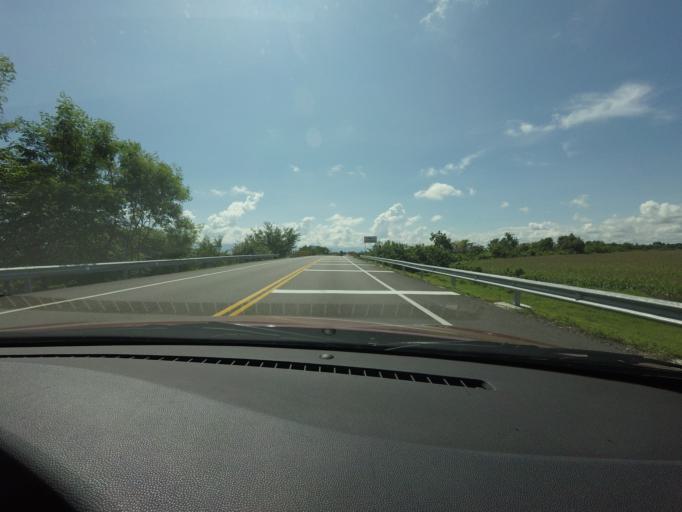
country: CO
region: Tolima
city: Espinal
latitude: 4.1464
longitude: -74.9121
